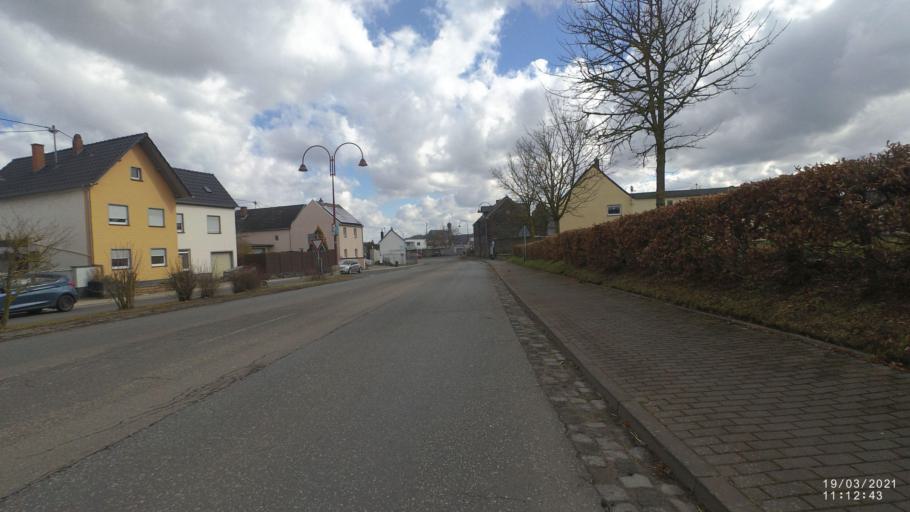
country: DE
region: Rheinland-Pfalz
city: Kruft
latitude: 50.3822
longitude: 7.3318
